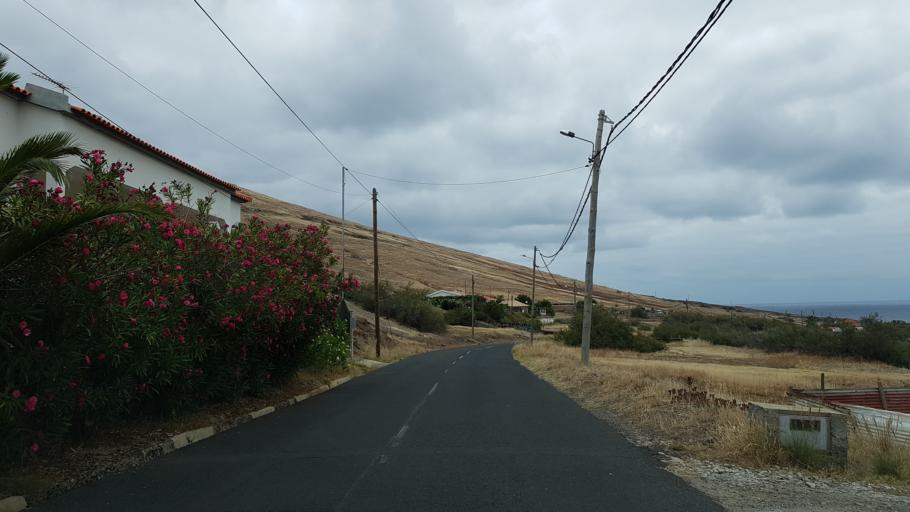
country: PT
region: Madeira
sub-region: Porto Santo
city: Vila de Porto Santo
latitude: 33.0723
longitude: -16.3067
